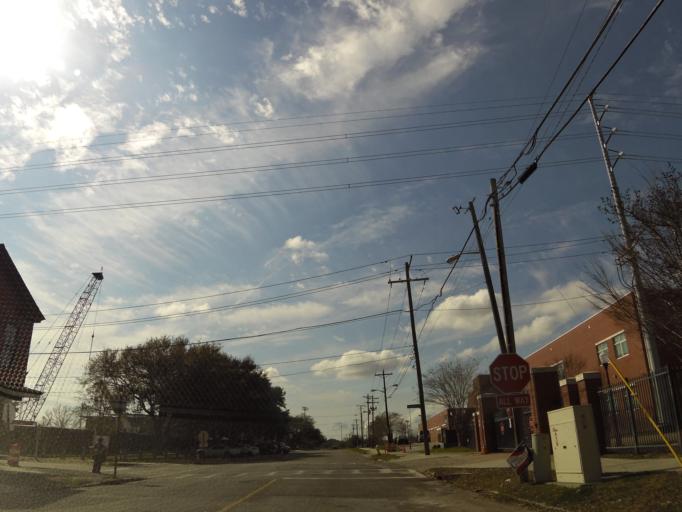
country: US
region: South Carolina
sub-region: Charleston County
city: Charleston
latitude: 32.7931
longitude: -79.9527
